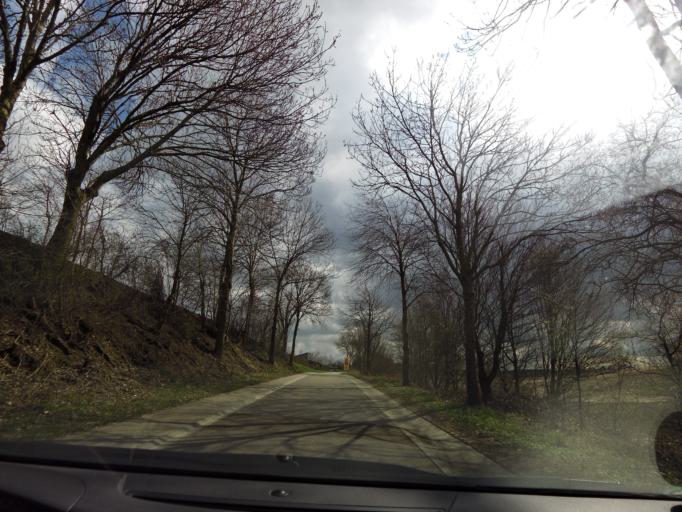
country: NL
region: Limburg
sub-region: Gemeente Voerendaal
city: Kunrade
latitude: 50.8627
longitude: 5.9138
